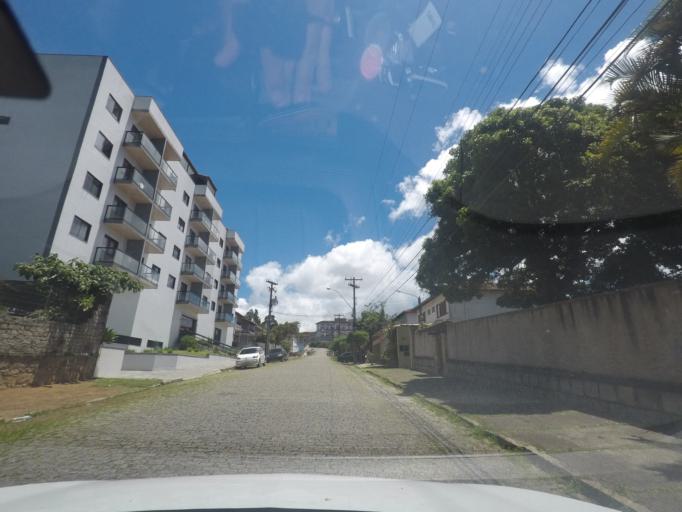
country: BR
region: Rio de Janeiro
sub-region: Teresopolis
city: Teresopolis
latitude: -22.4365
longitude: -42.9824
